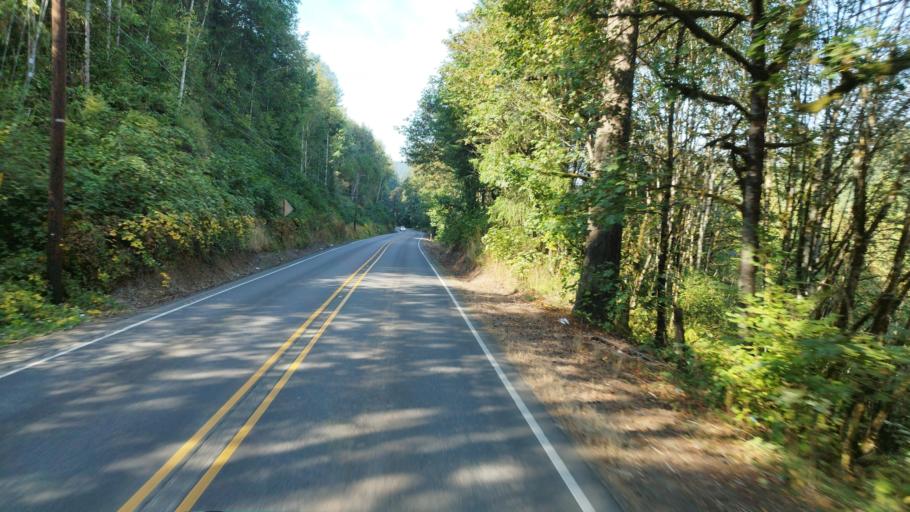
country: US
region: Oregon
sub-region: Washington County
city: Bethany
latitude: 45.6175
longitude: -122.8609
